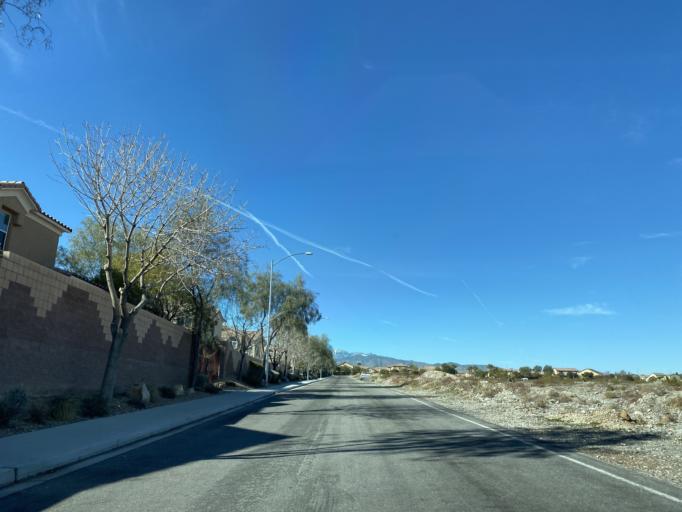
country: US
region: Nevada
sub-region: Clark County
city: Summerlin South
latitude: 36.3011
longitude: -115.3021
